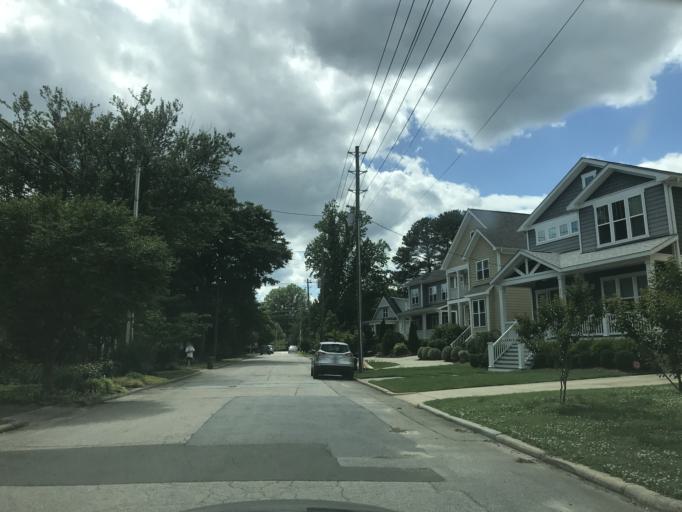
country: US
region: North Carolina
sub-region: Wake County
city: Raleigh
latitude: 35.8055
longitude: -78.6295
